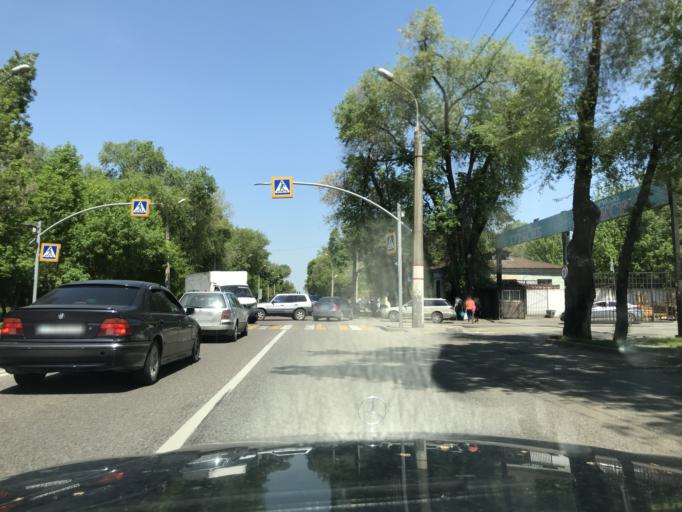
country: KZ
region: Almaty Oblysy
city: Pervomayskiy
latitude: 43.3258
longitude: 76.9594
